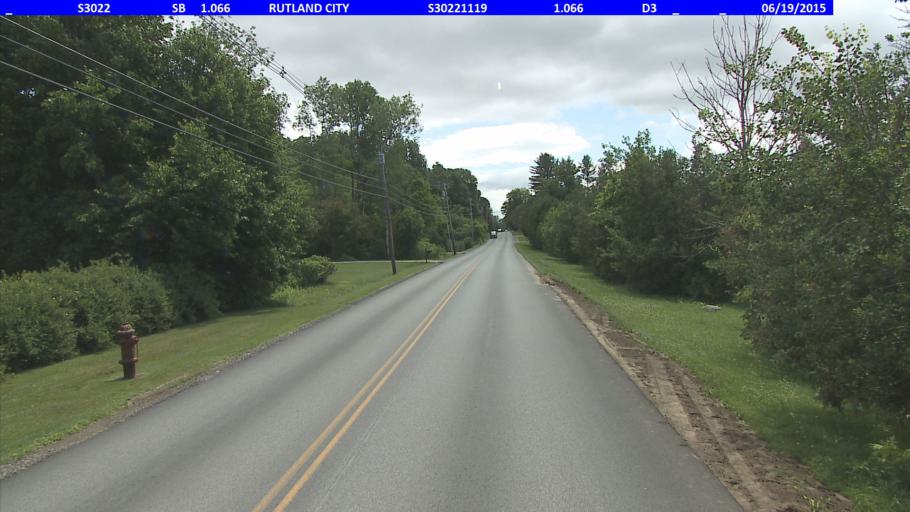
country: US
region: Vermont
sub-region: Rutland County
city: Rutland
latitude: 43.6239
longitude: -72.9855
